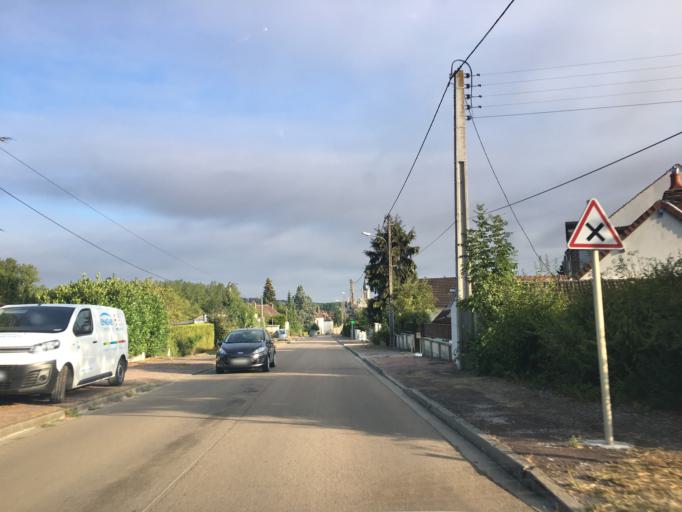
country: FR
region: Bourgogne
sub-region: Departement de l'Yonne
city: Aillant-sur-Tholon
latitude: 47.8704
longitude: 3.3530
